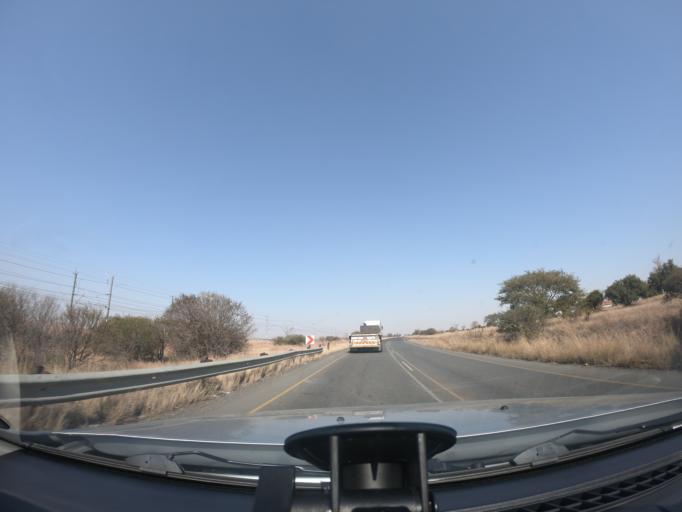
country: ZA
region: KwaZulu-Natal
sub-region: uThukela District Municipality
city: Ladysmith
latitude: -28.7544
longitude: 29.8226
